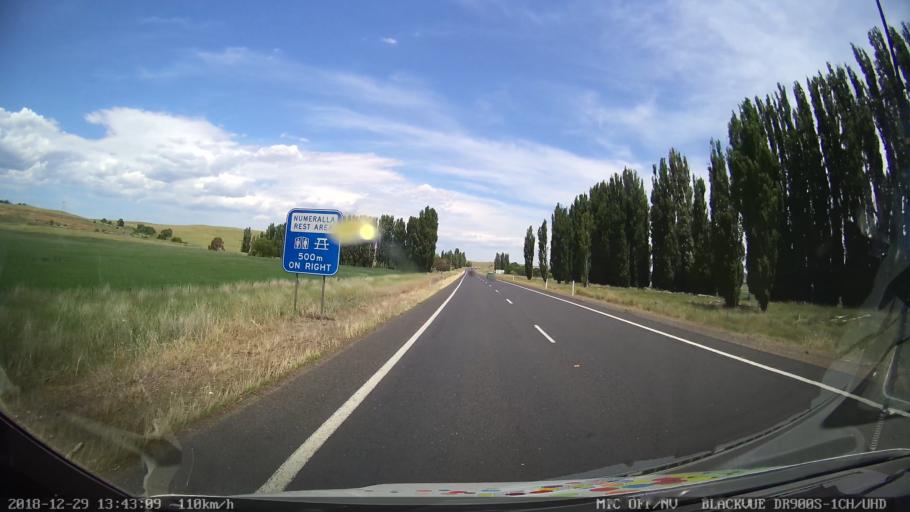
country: AU
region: New South Wales
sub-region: Cooma-Monaro
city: Cooma
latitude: -36.0681
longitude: 149.1585
